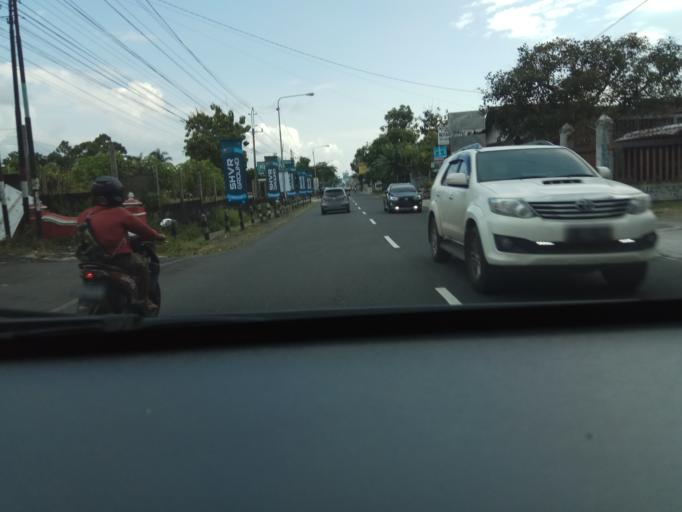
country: ID
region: Daerah Istimewa Yogyakarta
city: Melati
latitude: -7.7158
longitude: 110.4061
